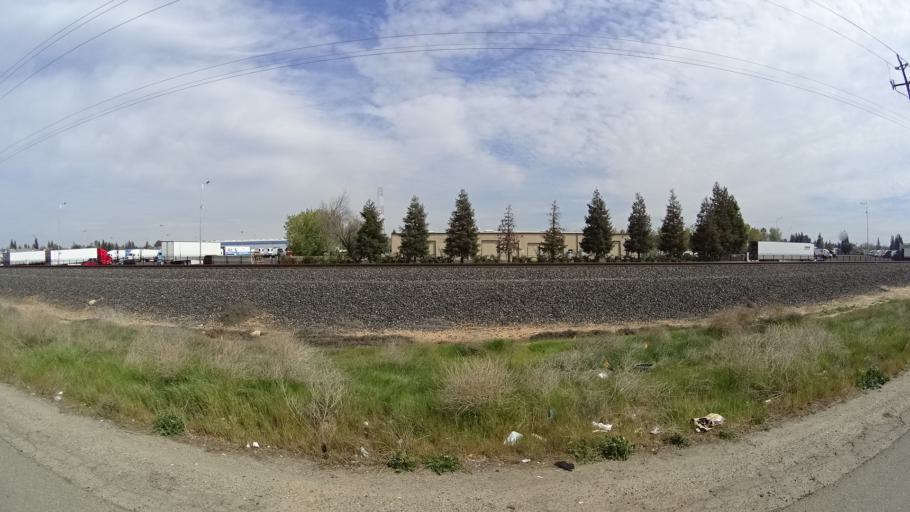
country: US
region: California
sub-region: Fresno County
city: West Park
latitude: 36.8134
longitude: -119.8849
